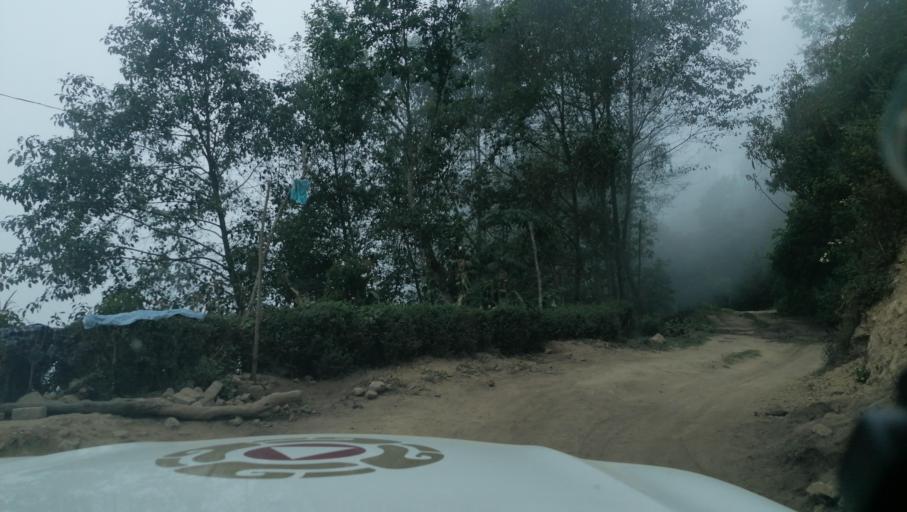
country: GT
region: San Marcos
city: Tacana
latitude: 15.2178
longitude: -92.1839
